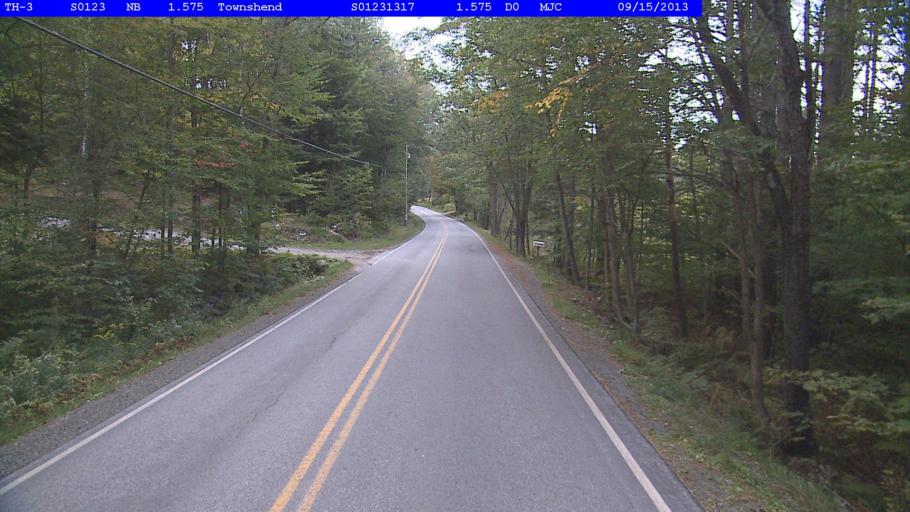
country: US
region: Vermont
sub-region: Windham County
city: Newfane
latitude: 43.1054
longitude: -72.7088
